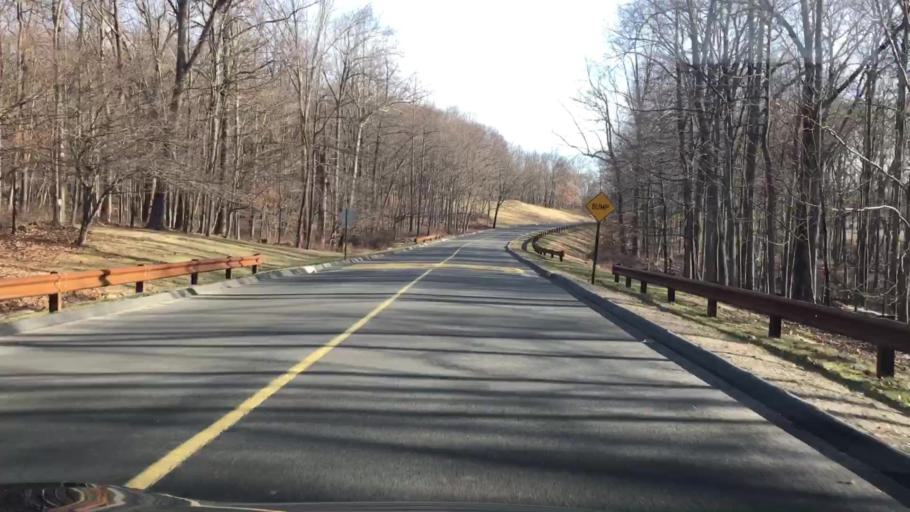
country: US
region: New York
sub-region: Putnam County
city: Peach Lake
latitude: 41.3744
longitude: -73.5201
